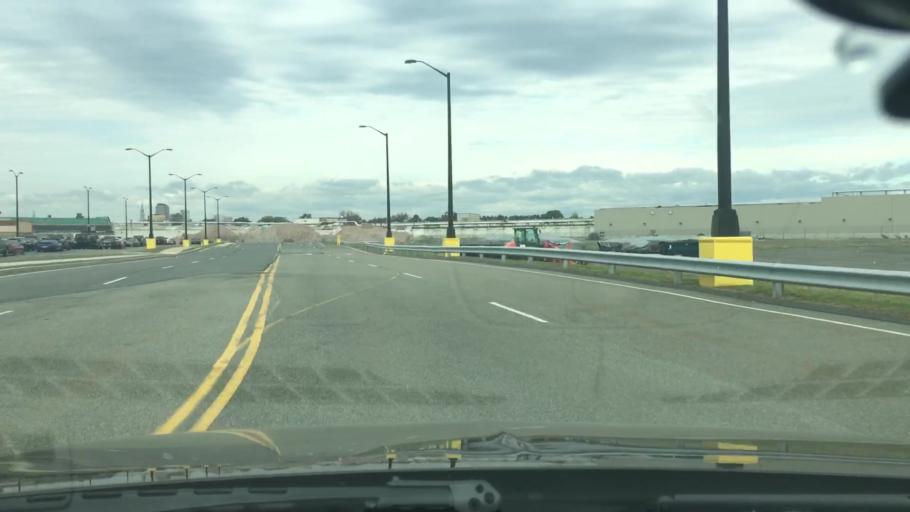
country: US
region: Connecticut
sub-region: Hartford County
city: East Hartford
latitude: 41.7489
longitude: -72.6303
